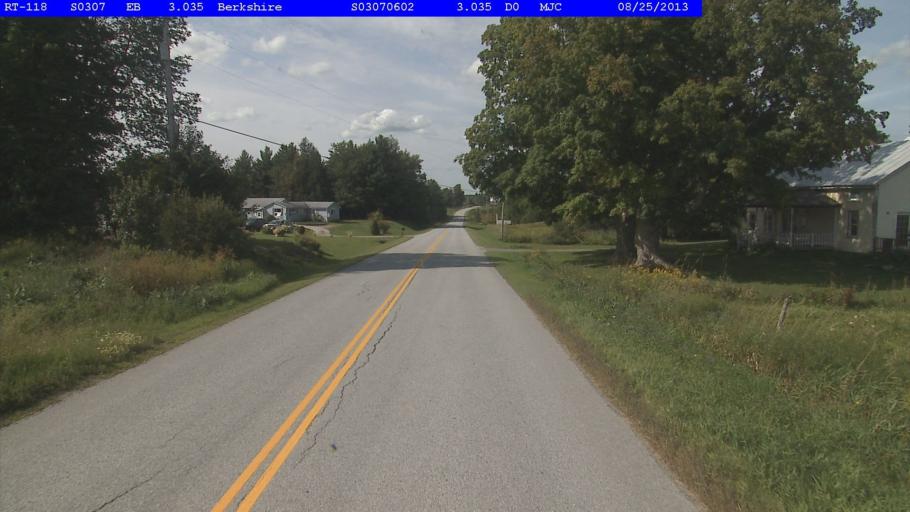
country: US
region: Vermont
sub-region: Franklin County
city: Enosburg Falls
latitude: 44.9594
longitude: -72.7566
